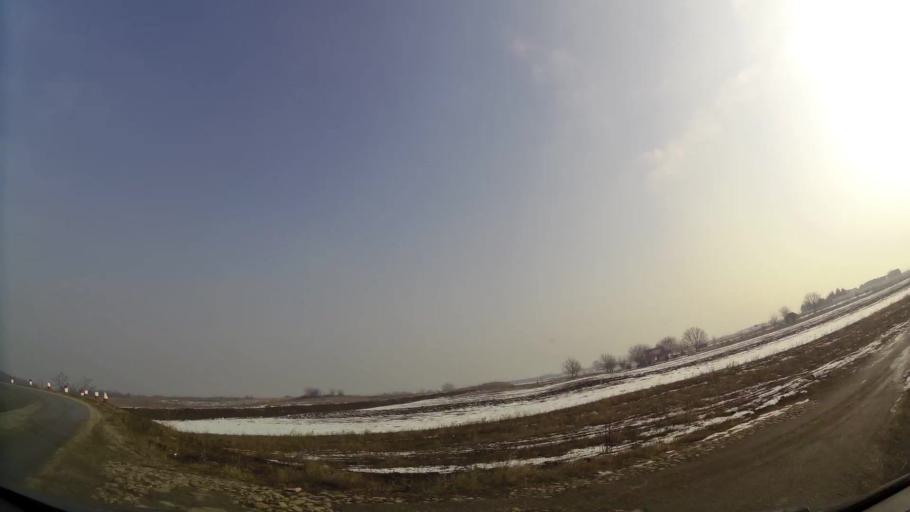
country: MK
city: Kadino
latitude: 41.9726
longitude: 21.6065
